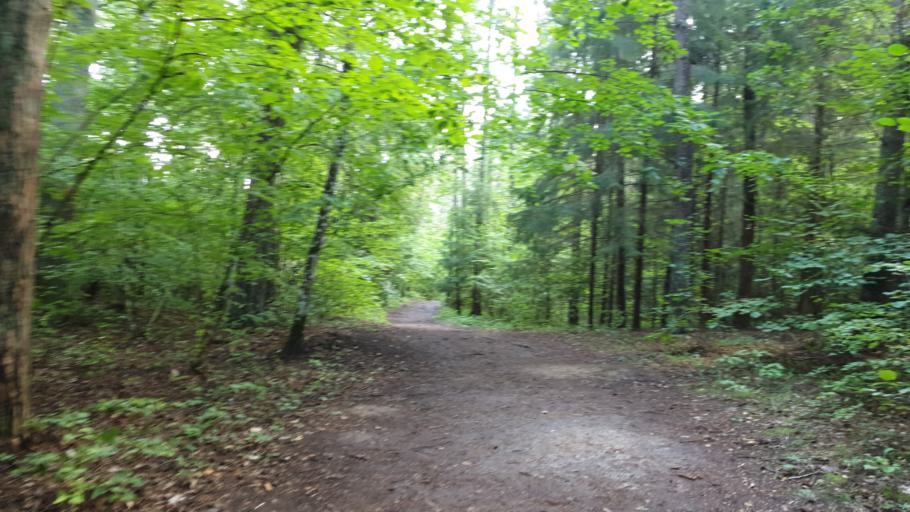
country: LT
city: Trakai
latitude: 54.6459
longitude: 24.9667
